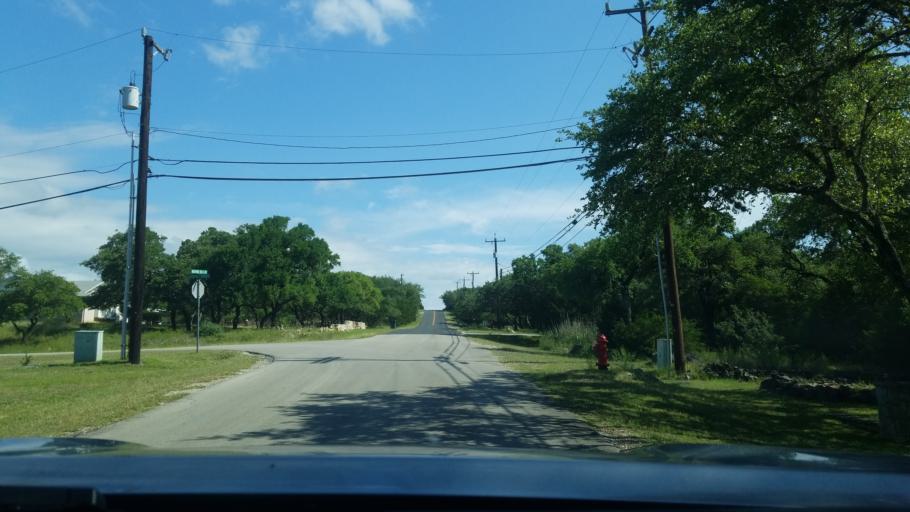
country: US
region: Texas
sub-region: Comal County
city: Bulverde
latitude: 29.7450
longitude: -98.4427
